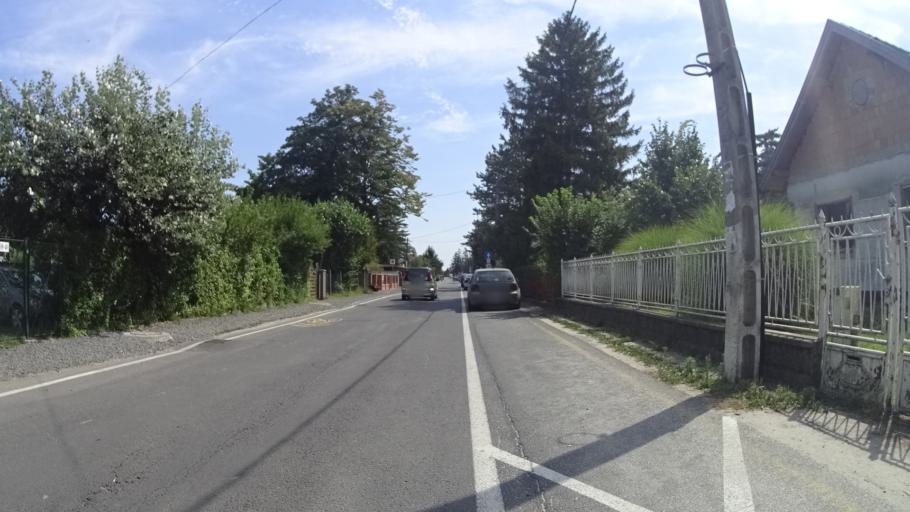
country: HU
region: Somogy
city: Balatonbereny
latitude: 46.7048
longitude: 17.3775
